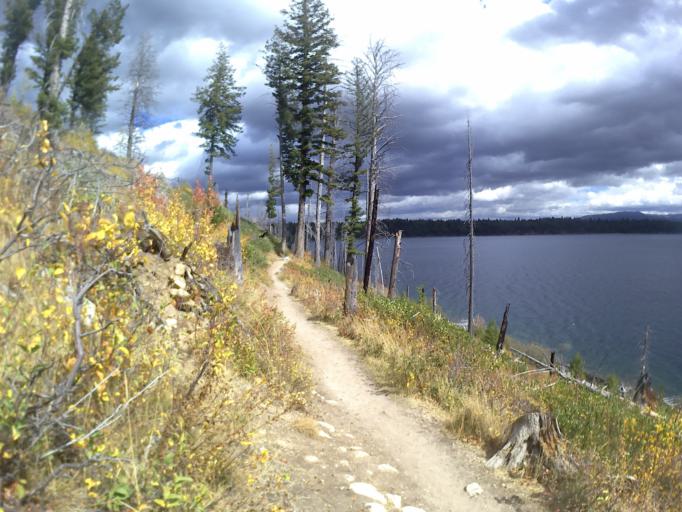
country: US
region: Wyoming
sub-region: Teton County
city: Moose Wilson Road
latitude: 43.7743
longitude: -110.7374
